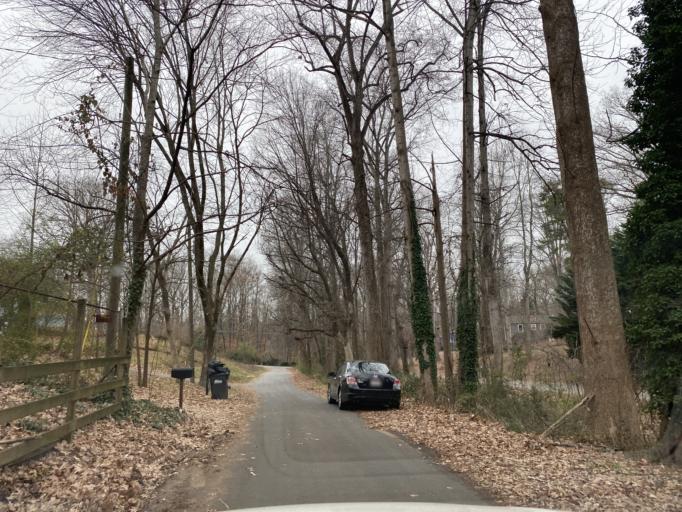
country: US
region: Georgia
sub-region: Cobb County
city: Fair Oaks
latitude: 33.9006
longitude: -84.5738
